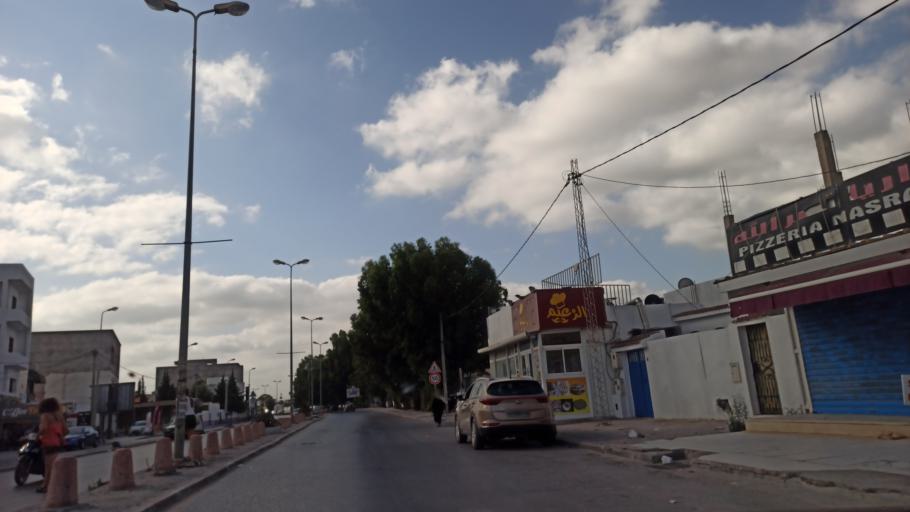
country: TN
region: Tunis
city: La Goulette
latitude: 36.8527
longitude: 10.2579
